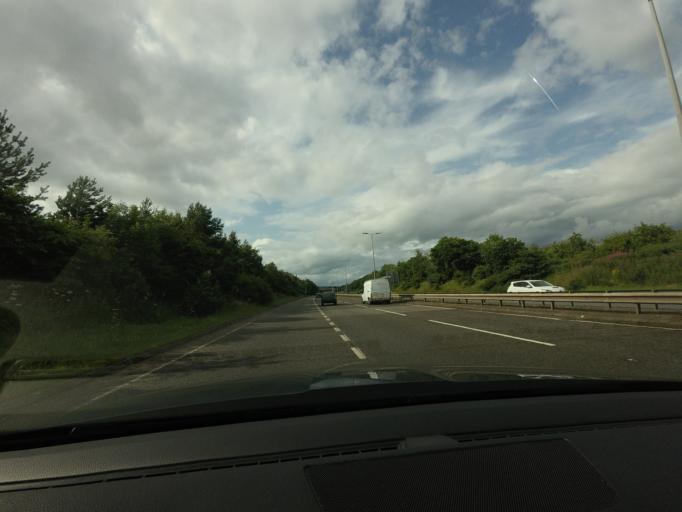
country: GB
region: Scotland
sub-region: Highland
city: Inverness
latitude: 57.4750
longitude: -4.1872
